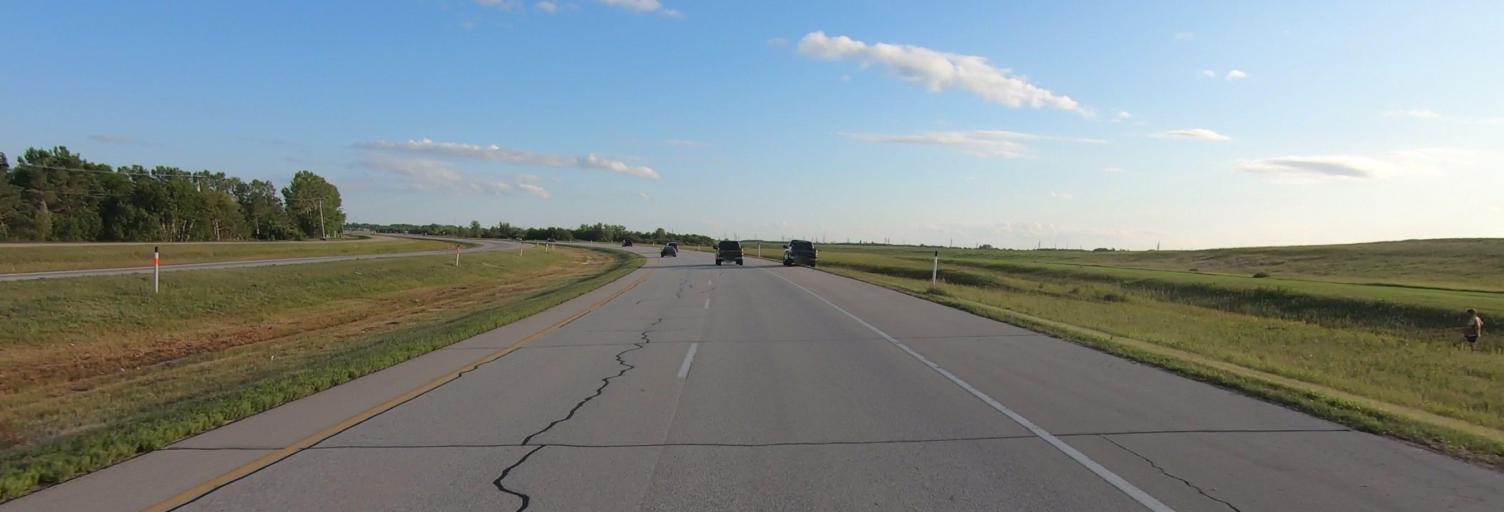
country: CA
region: Manitoba
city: Selkirk
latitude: 49.9915
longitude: -96.9769
